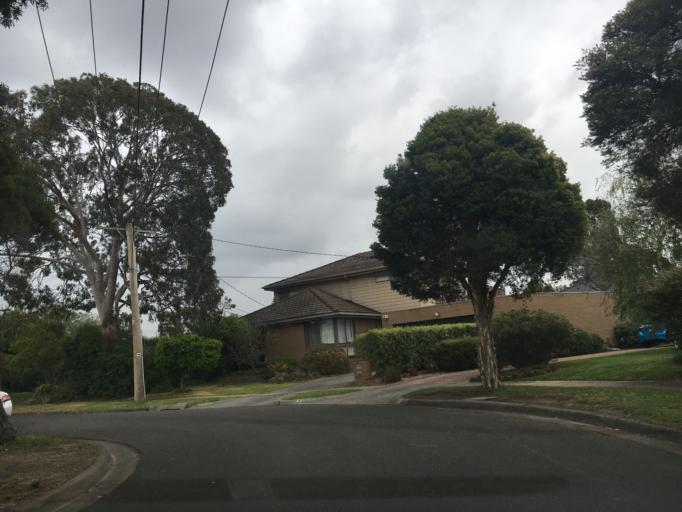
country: AU
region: Victoria
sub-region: Whitehorse
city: Vermont South
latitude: -37.8724
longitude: 145.1783
